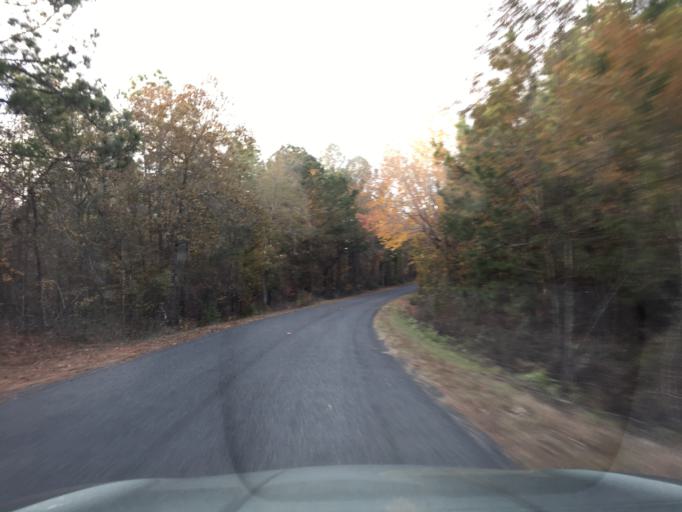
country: US
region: South Carolina
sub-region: Lexington County
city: Leesville
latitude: 33.6774
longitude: -81.3743
